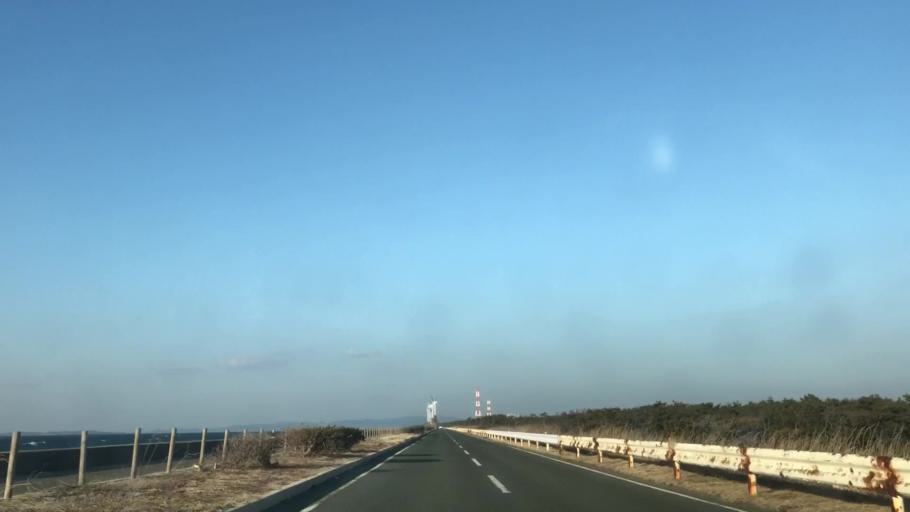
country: JP
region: Aichi
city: Toyohama
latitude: 34.6188
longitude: 137.0414
